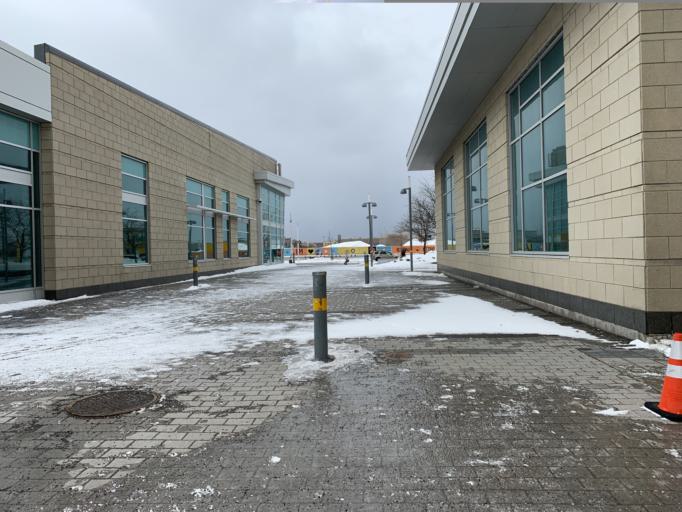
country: CA
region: Quebec
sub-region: Laval
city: Laval
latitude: 45.5583
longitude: -73.7212
